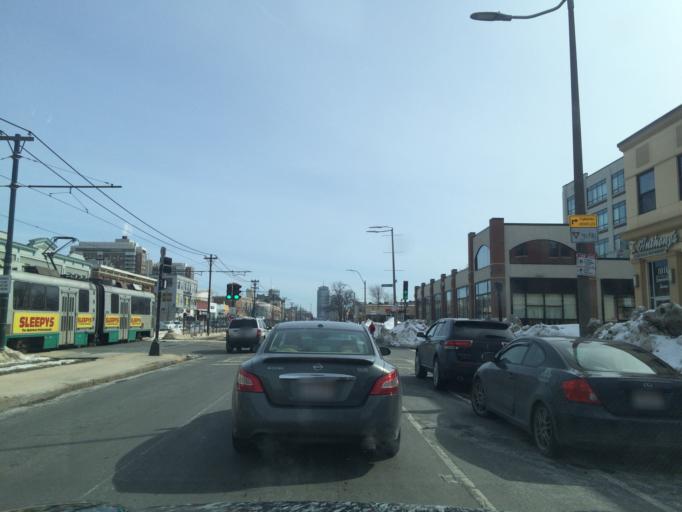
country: US
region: Massachusetts
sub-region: Norfolk County
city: Brookline
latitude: 42.3517
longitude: -71.1217
